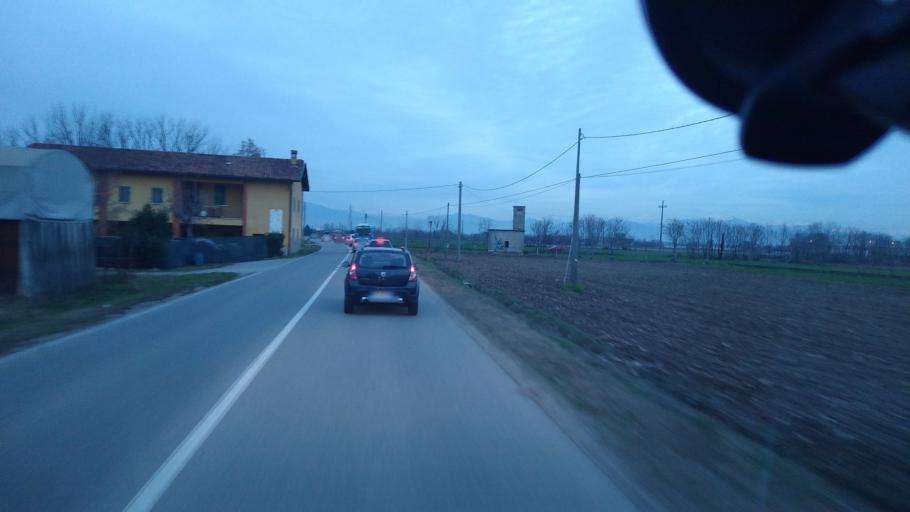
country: IT
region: Lombardy
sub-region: Provincia di Bergamo
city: Pontirolo Nuovo
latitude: 45.5601
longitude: 9.5845
